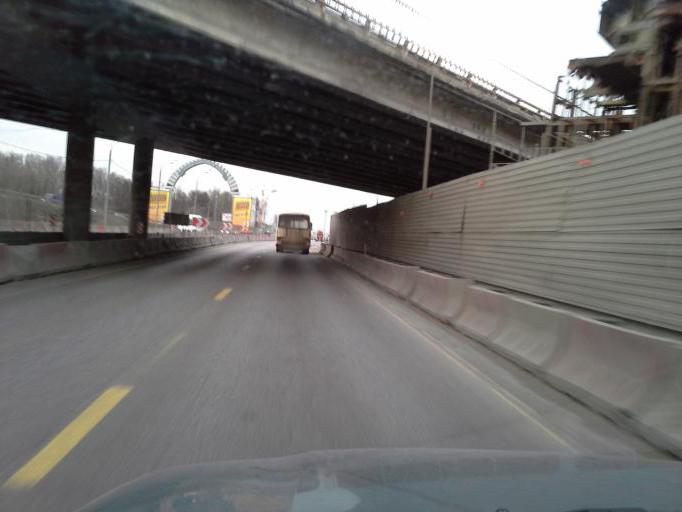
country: RU
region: Moskovskaya
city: Novoivanovskoye
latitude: 55.6938
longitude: 37.3375
